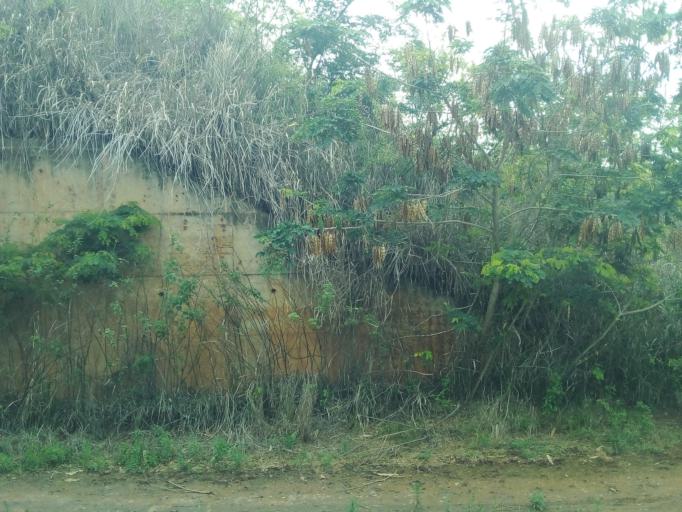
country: BR
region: Minas Gerais
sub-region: Governador Valadares
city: Governador Valadares
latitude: -19.0814
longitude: -42.1604
